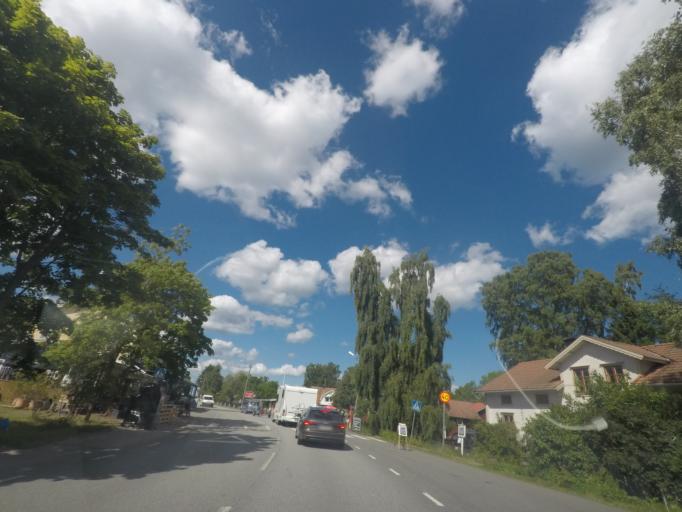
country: SE
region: Stockholm
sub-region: Norrtalje Kommun
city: Arno
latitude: 60.1002
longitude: 18.8090
